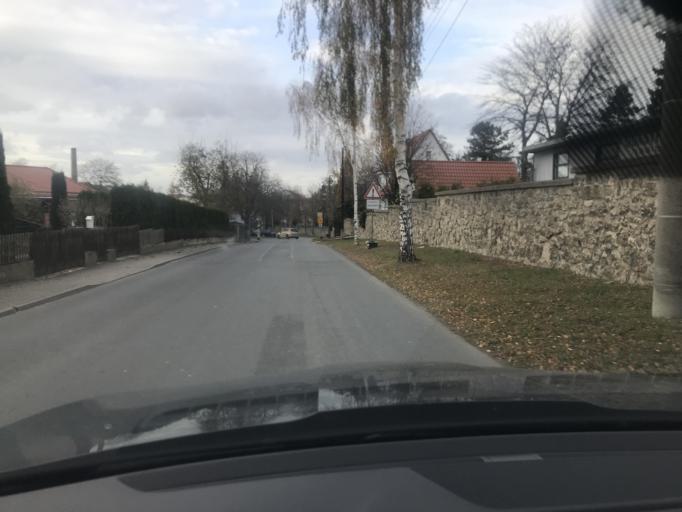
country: DE
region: Saxony-Anhalt
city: Quedlinburg
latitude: 51.7870
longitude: 11.1648
